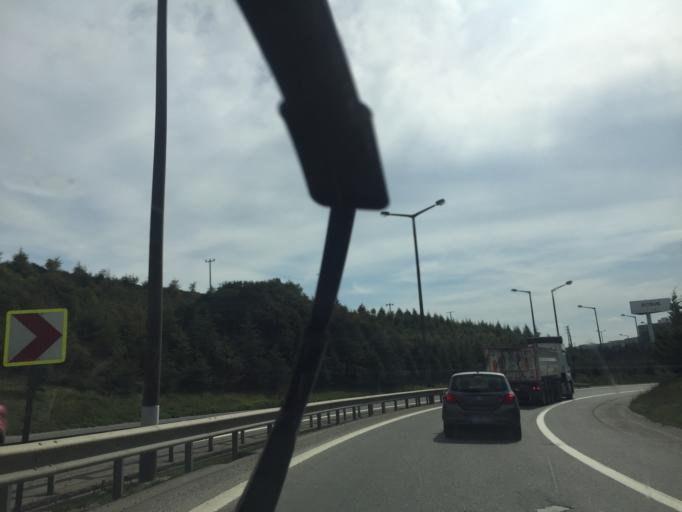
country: TR
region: Kocaeli
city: Balcik
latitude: 40.8704
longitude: 29.3986
